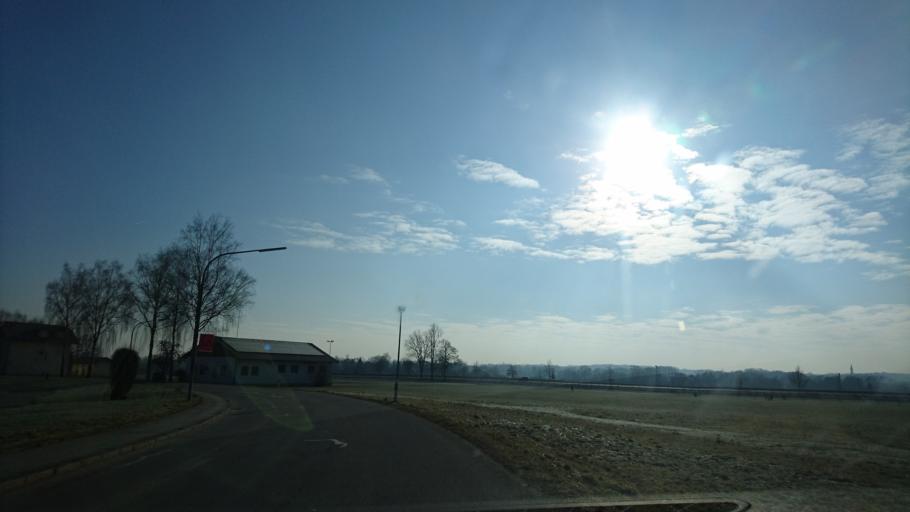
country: DE
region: Bavaria
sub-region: Lower Bavaria
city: Bad Griesbach
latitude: 48.4167
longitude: 13.2148
